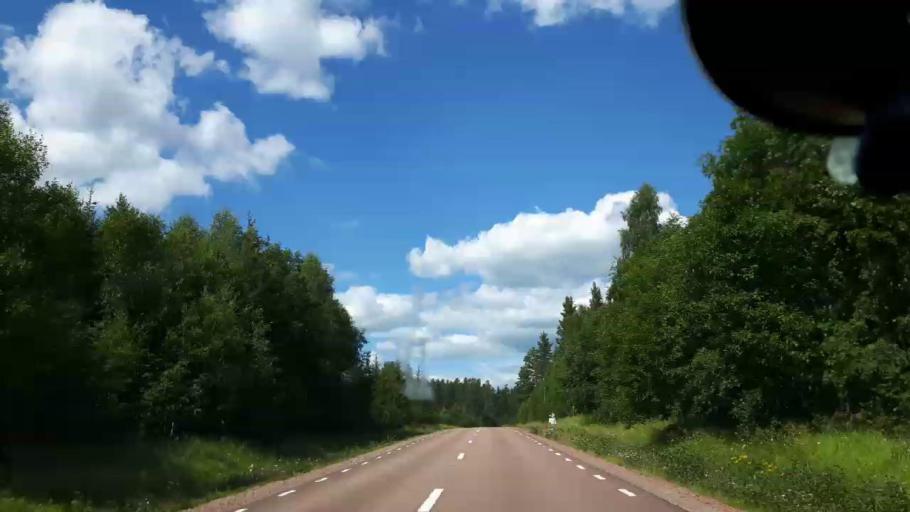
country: SE
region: Jaemtland
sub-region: Ragunda Kommun
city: Hammarstrand
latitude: 63.0316
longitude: 16.5212
